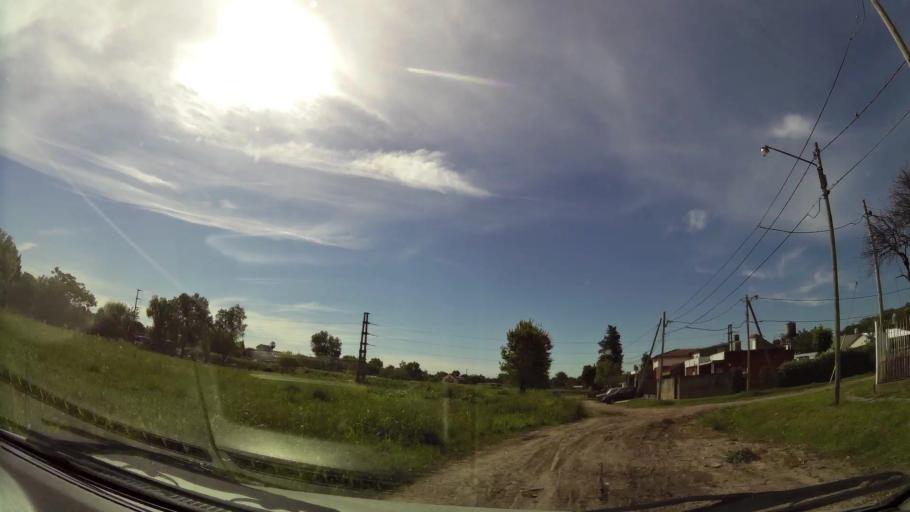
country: AR
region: Buenos Aires
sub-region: Partido de Almirante Brown
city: Adrogue
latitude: -34.8114
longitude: -58.3541
